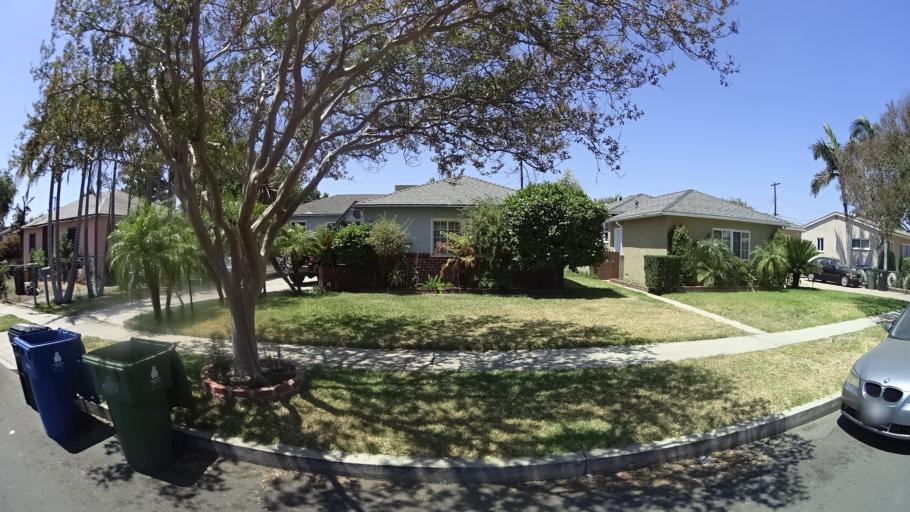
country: US
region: California
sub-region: Los Angeles County
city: San Fernando
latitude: 34.2349
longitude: -118.4314
